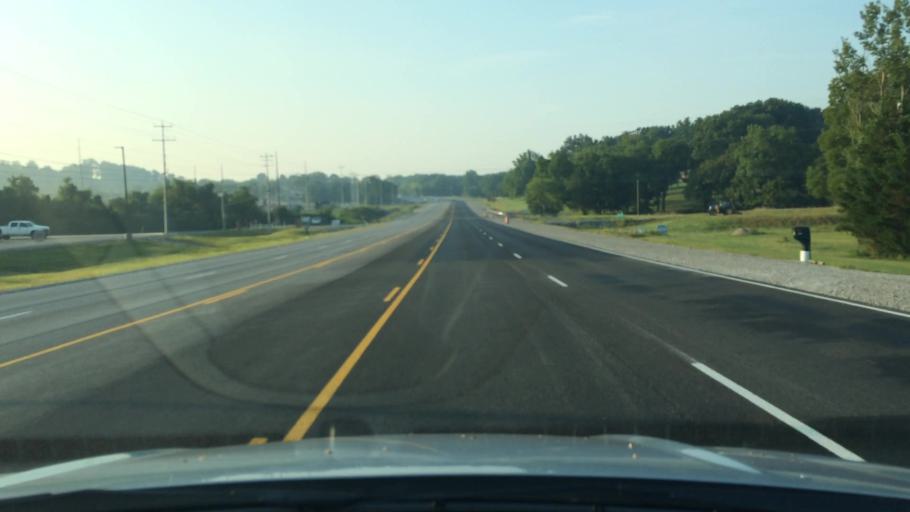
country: US
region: Tennessee
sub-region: Giles County
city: Pulaski
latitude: 35.1512
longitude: -87.0030
